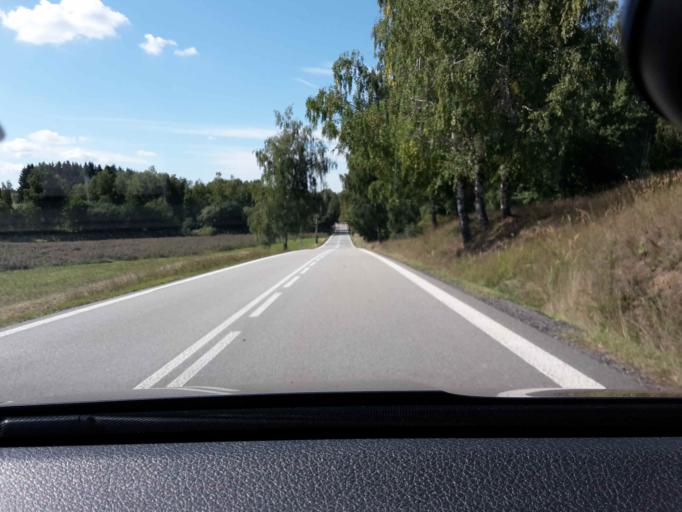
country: CZ
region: Jihocesky
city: Strmilov
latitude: 49.1656
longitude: 15.2207
